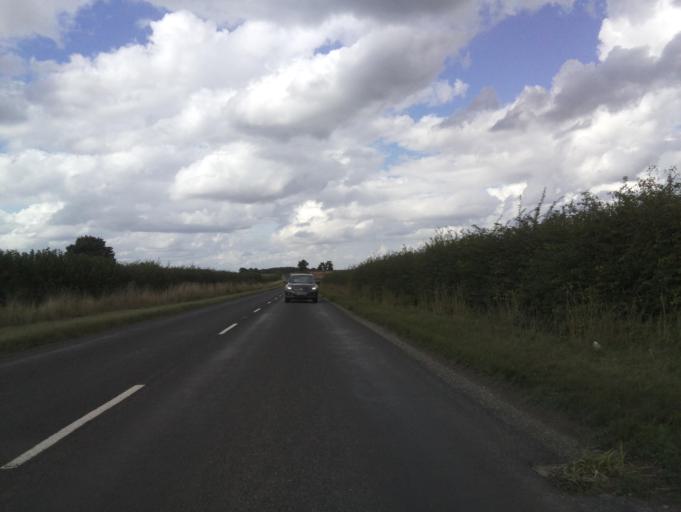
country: GB
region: England
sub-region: North Yorkshire
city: Ripon
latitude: 54.1672
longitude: -1.5500
